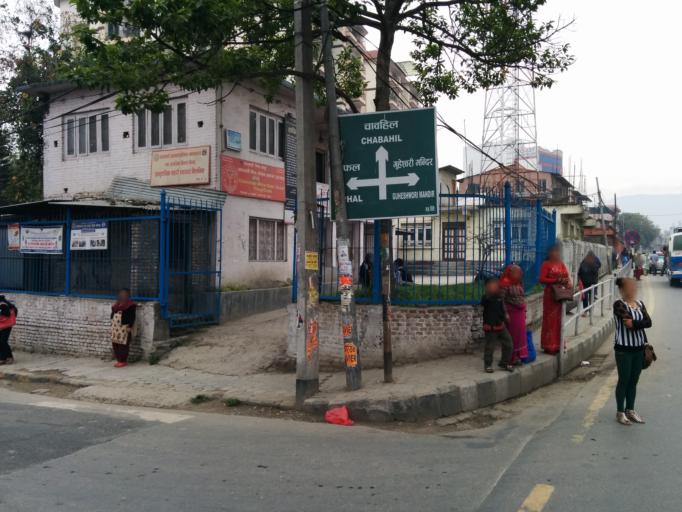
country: NP
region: Central Region
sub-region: Bagmati Zone
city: Kathmandu
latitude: 27.7131
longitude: 85.3453
